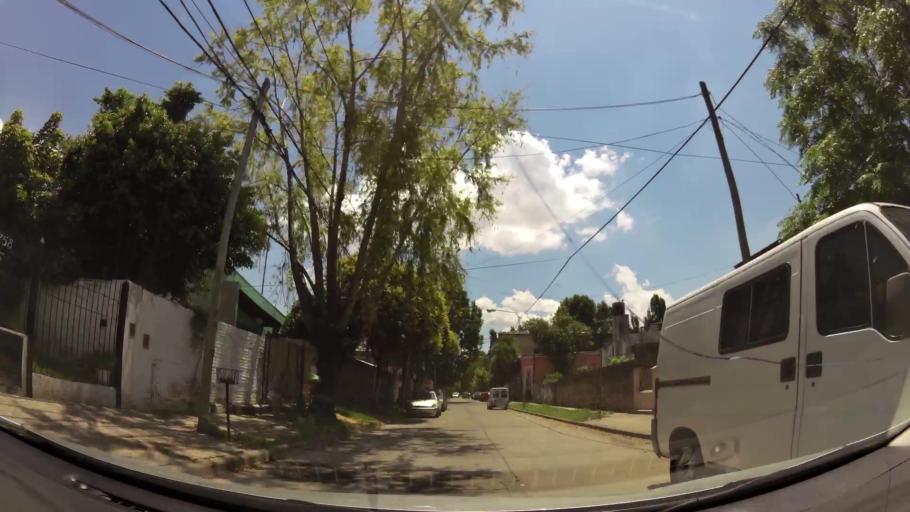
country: AR
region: Buenos Aires
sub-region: Partido de Tigre
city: Tigre
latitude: -34.4201
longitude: -58.5899
